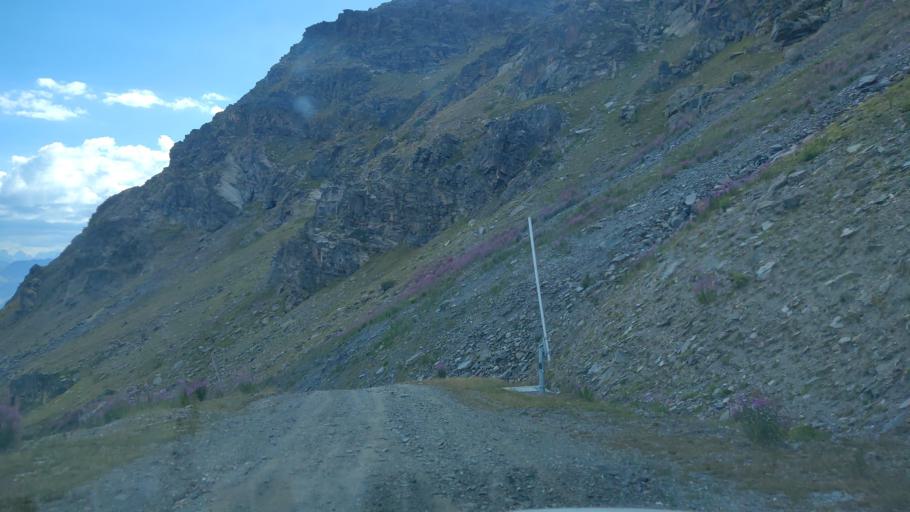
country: FR
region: Rhone-Alpes
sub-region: Departement de la Savoie
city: Val Thorens
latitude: 45.2529
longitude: 6.5648
